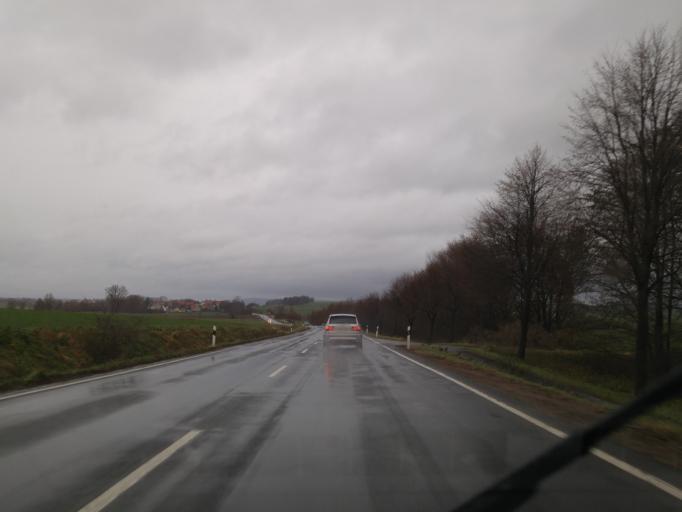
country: DE
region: Lower Saxony
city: Gemeinde Friedland
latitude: 51.4474
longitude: 9.9320
